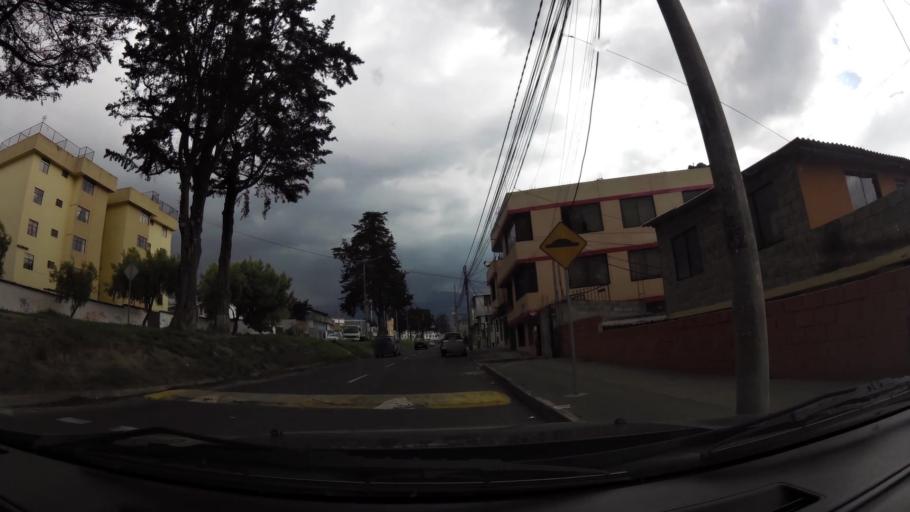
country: EC
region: Pichincha
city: Quito
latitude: -0.0865
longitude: -78.4745
